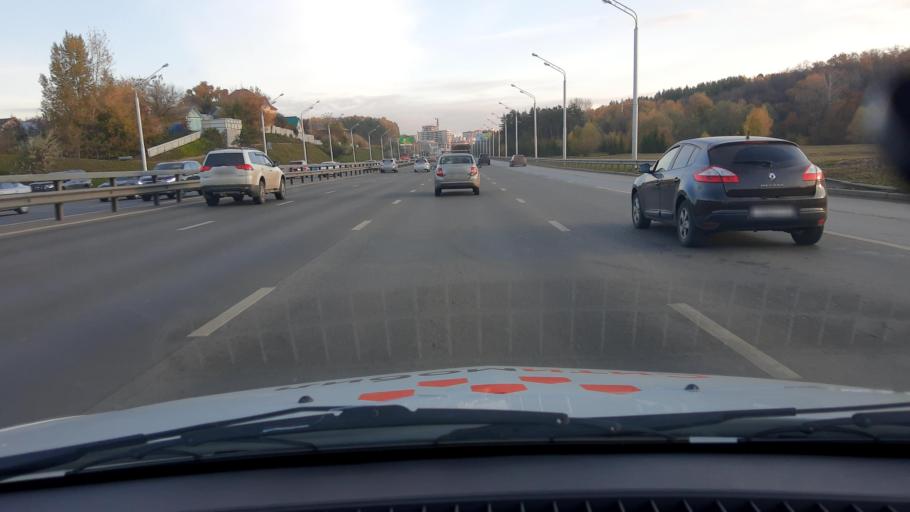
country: RU
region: Bashkortostan
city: Ufa
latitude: 54.7390
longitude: 56.0091
